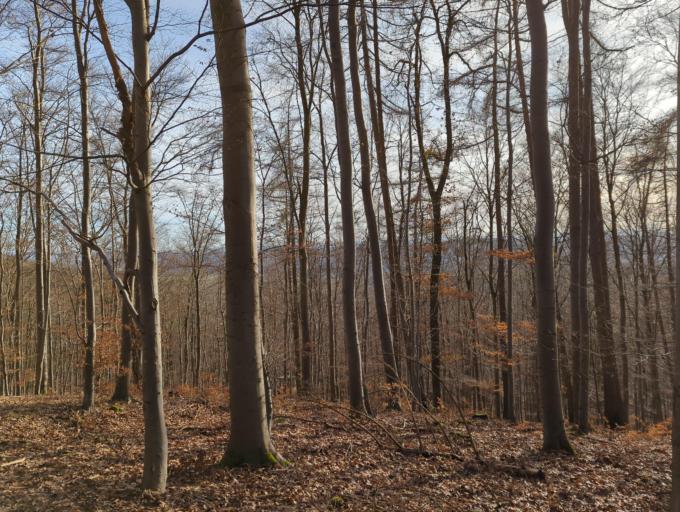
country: DE
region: Saxony-Anhalt
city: Stolberg
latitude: 51.5522
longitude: 10.9156
